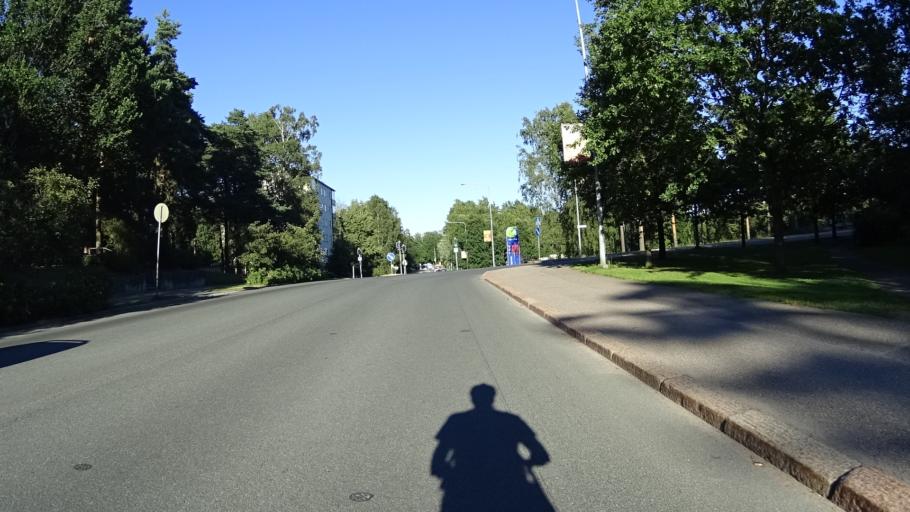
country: FI
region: Uusimaa
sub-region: Helsinki
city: Teekkarikylae
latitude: 60.2037
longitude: 24.8714
